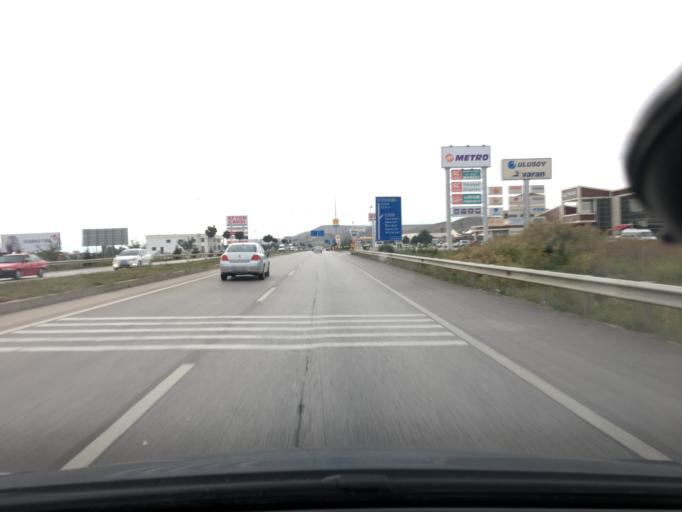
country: TR
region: Afyonkarahisar
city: Afyonkarahisar
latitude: 38.7951
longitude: 30.3981
